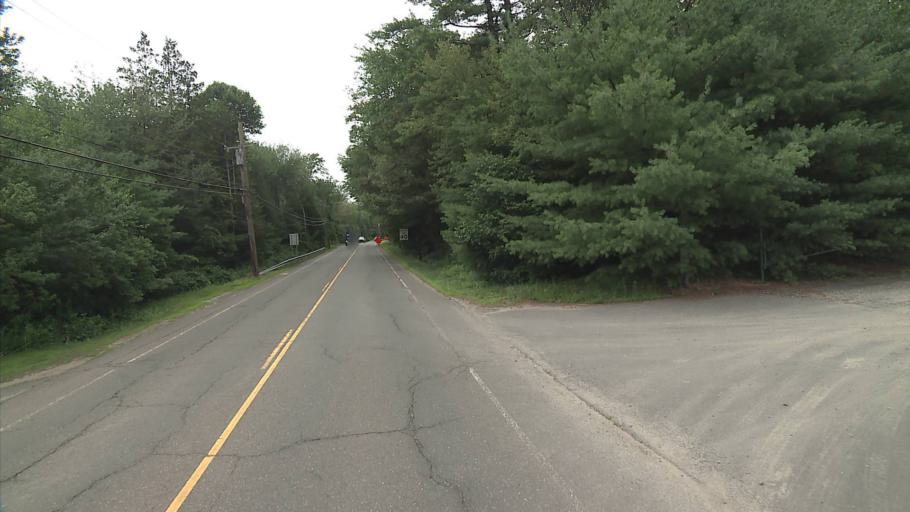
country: US
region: Connecticut
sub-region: Middlesex County
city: Clinton
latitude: 41.3571
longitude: -72.5568
